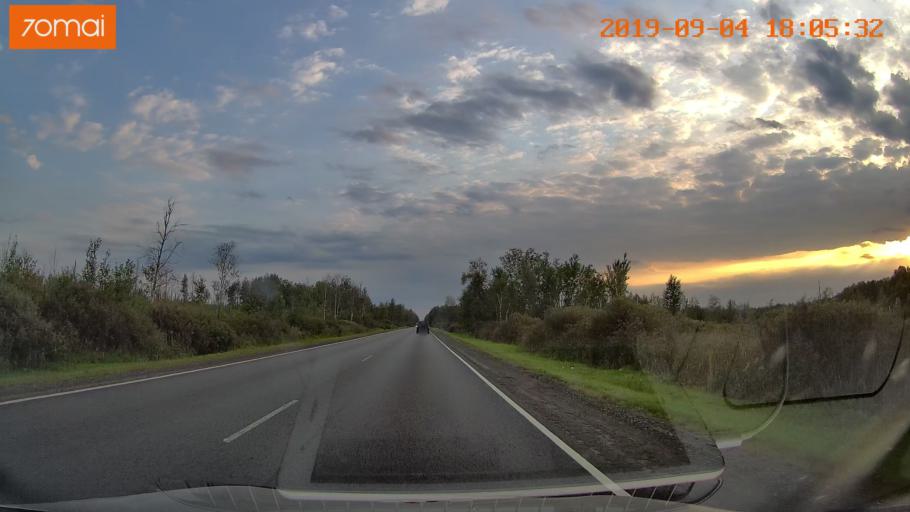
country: RU
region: Moskovskaya
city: Il'inskiy Pogost
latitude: 55.4404
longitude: 38.8255
